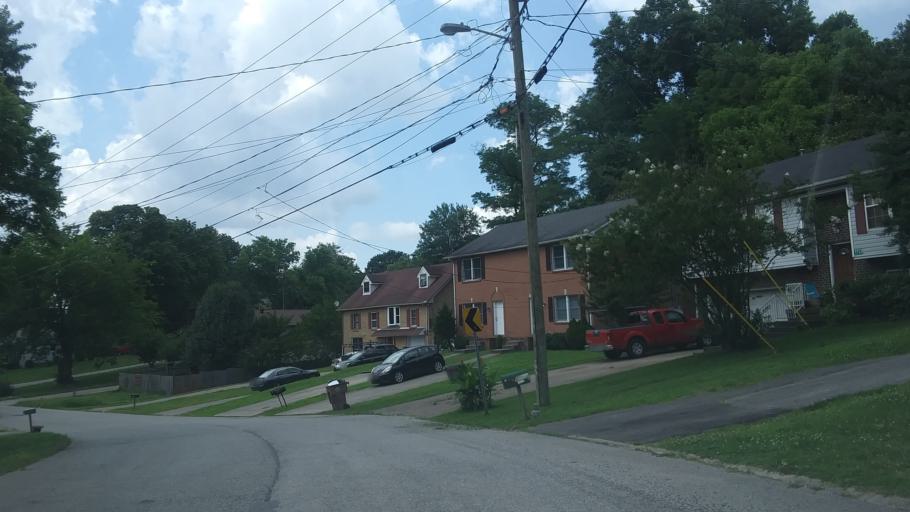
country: US
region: Tennessee
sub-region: Davidson County
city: Oak Hill
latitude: 36.0729
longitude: -86.7102
